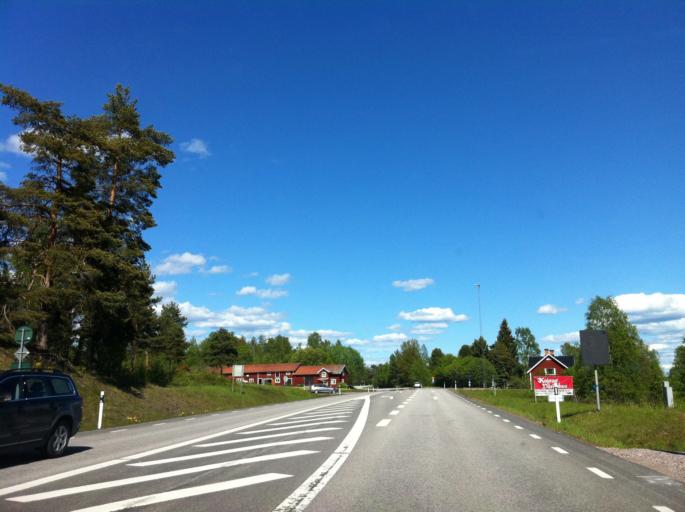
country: SE
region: Dalarna
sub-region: Rattviks Kommun
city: Vikarbyn
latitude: 60.9080
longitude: 15.0028
